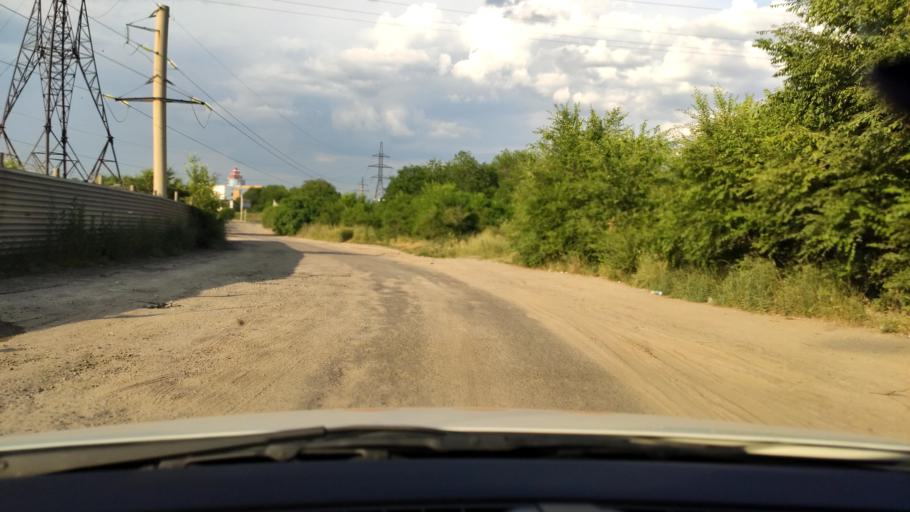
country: RU
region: Voronezj
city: Pridonskoy
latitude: 51.6645
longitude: 39.1252
